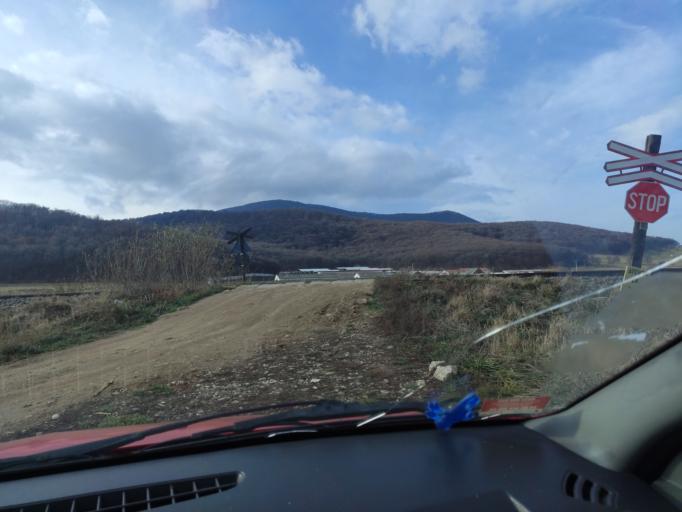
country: RO
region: Brasov
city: Codlea
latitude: 45.7185
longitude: 25.4577
